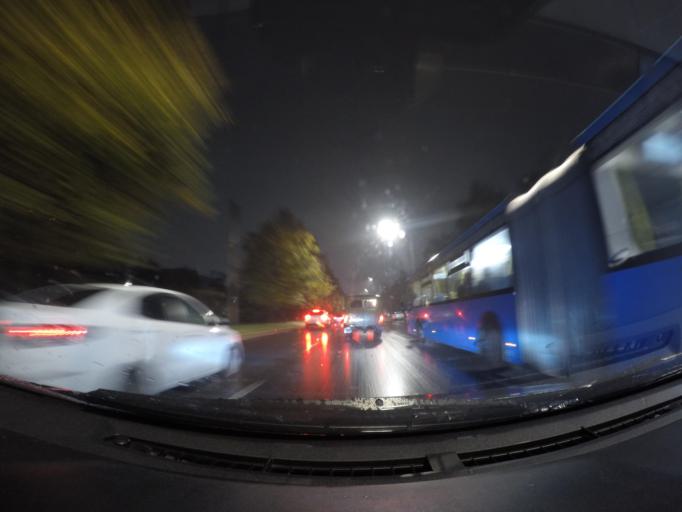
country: RU
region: Moscow
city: Kolomenskoye
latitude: 55.6741
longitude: 37.6634
